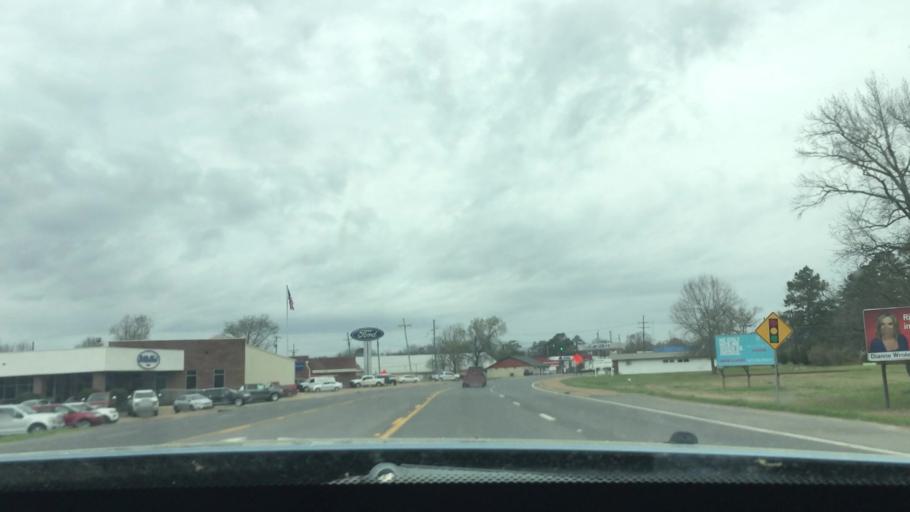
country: US
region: Louisiana
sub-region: Franklin Parish
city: Winnsboro
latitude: 32.1552
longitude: -91.7127
